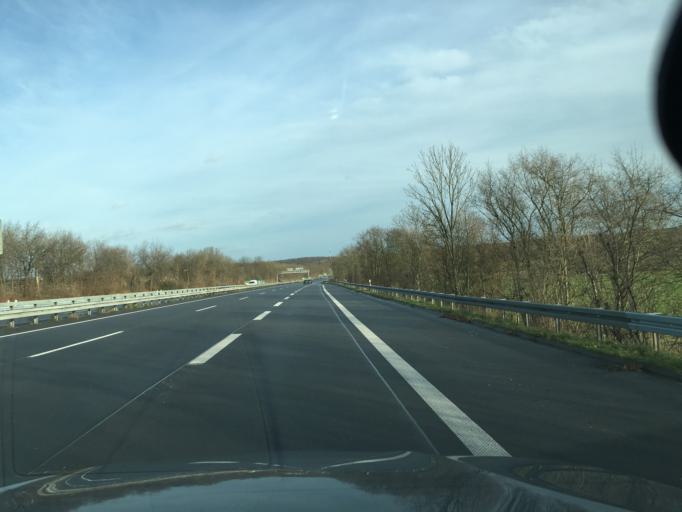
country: DE
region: North Rhine-Westphalia
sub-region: Regierungsbezirk Koln
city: Weilerswist
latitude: 50.7719
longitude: 6.8265
